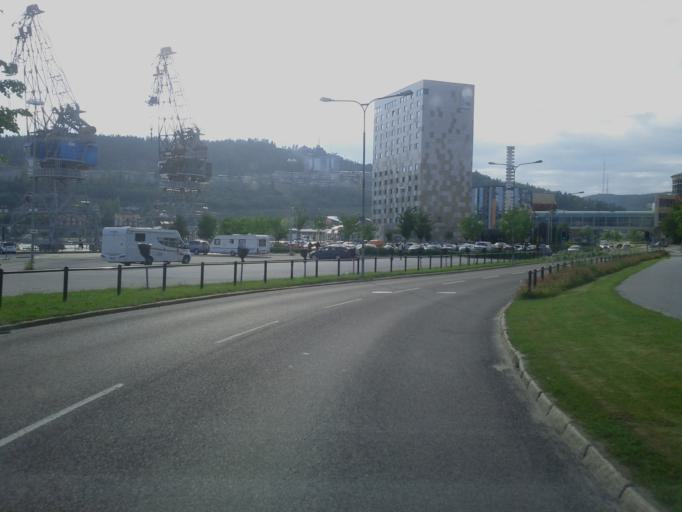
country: SE
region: Vaesternorrland
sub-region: OErnskoeldsviks Kommun
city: Ornskoldsvik
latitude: 63.2869
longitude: 18.7172
